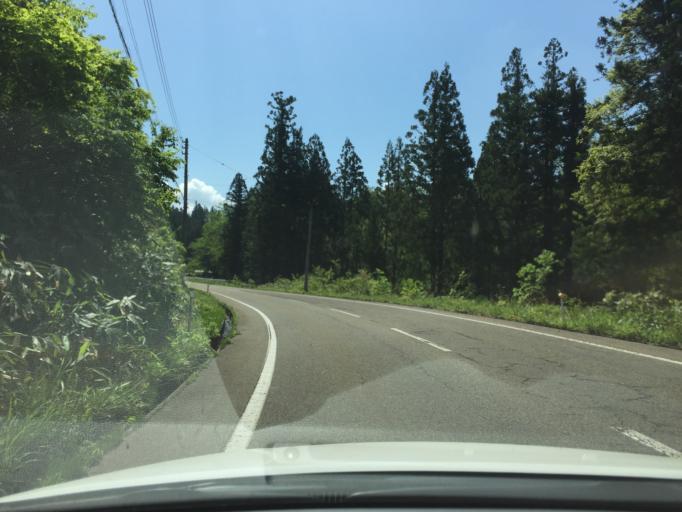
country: JP
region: Niigata
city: Tochio-honcho
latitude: 37.5322
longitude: 139.0927
